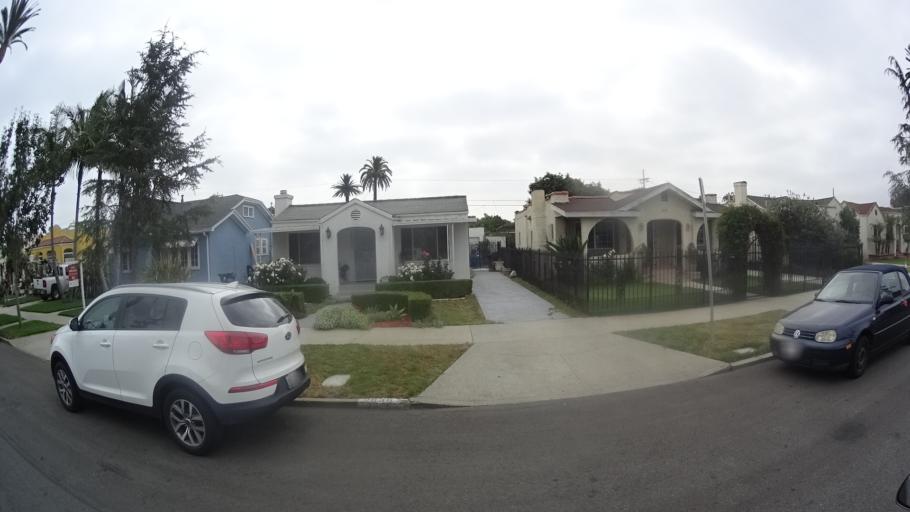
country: US
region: California
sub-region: Los Angeles County
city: View Park-Windsor Hills
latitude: 34.0301
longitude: -118.3395
